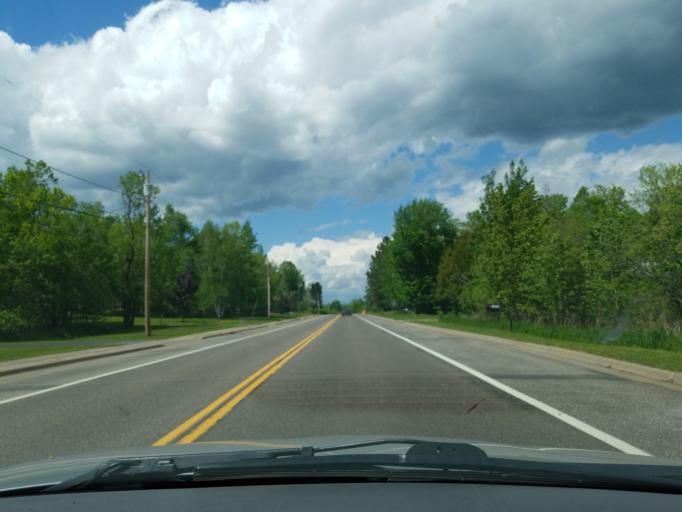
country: US
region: Minnesota
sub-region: Saint Louis County
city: Proctor
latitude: 46.7593
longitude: -92.2222
